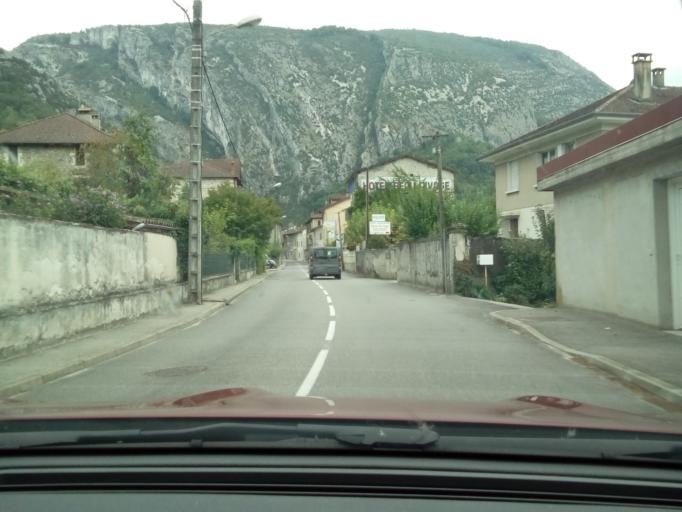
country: FR
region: Rhone-Alpes
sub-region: Departement de l'Isere
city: Pont-en-Royans
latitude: 45.0632
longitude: 5.3387
